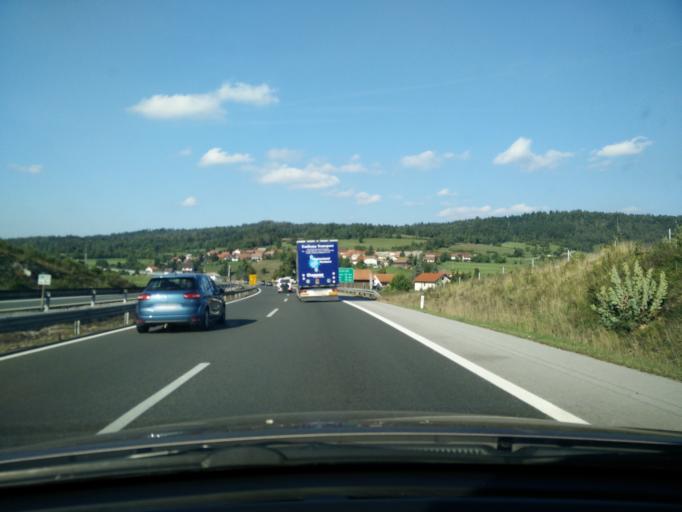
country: SI
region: Cerknica
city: Rakek
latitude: 45.8299
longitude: 14.2937
